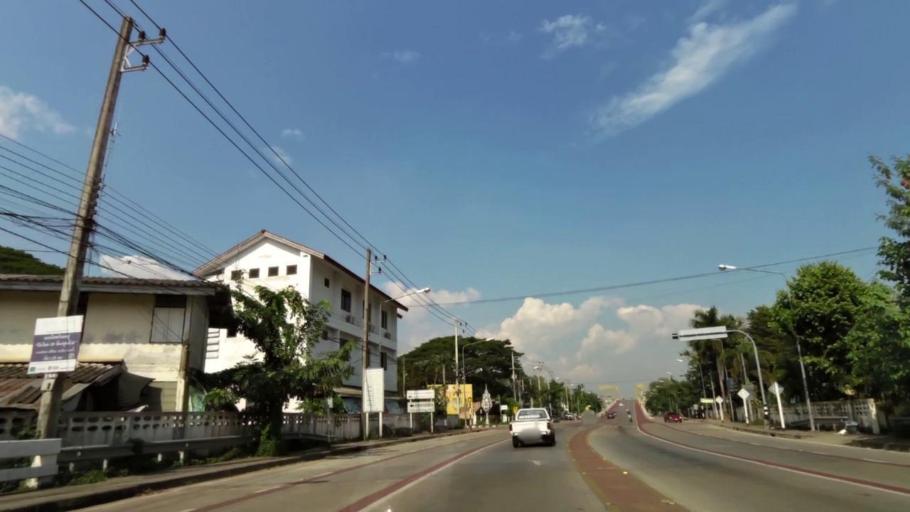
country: TH
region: Chiang Rai
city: Chiang Rai
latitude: 19.9142
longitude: 99.8323
